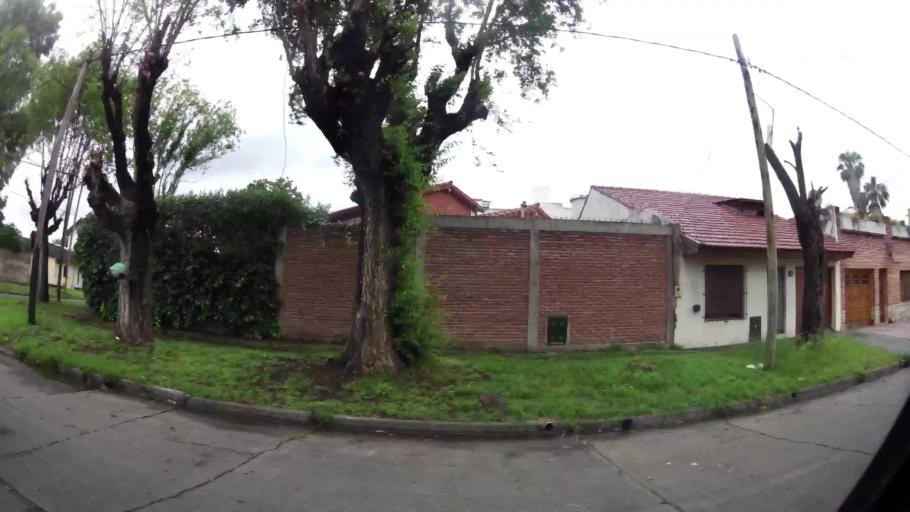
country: AR
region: Buenos Aires
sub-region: Partido de Lomas de Zamora
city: Lomas de Zamora
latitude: -34.7455
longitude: -58.3774
